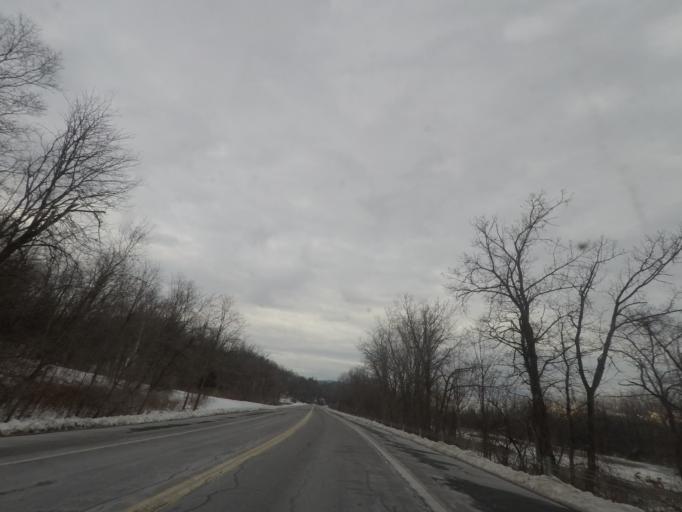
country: US
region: New York
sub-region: Rensselaer County
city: Castleton-on-Hudson
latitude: 42.5586
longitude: -73.7455
